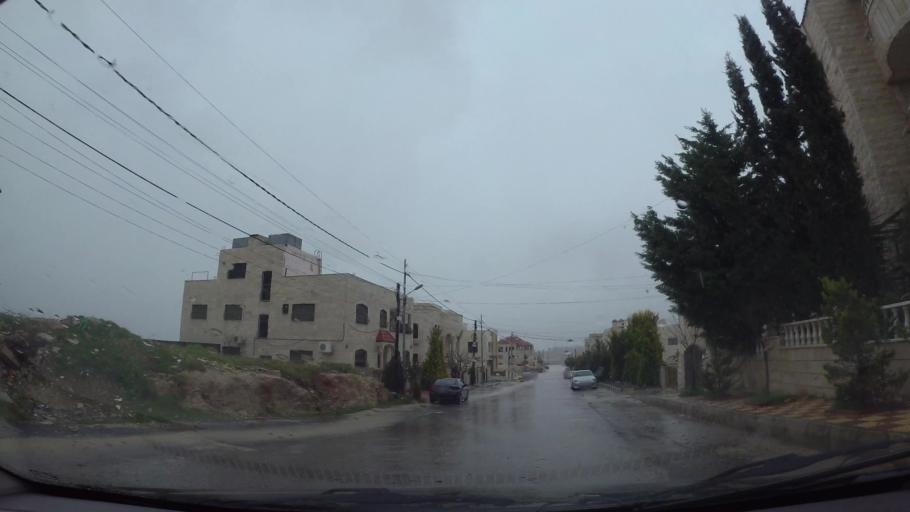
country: JO
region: Amman
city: Al Jubayhah
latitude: 32.0130
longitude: 35.9027
